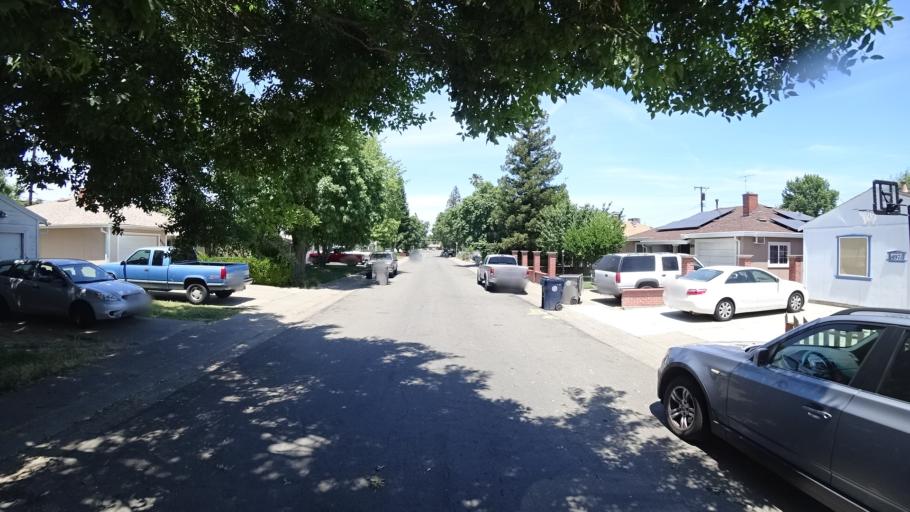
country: US
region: California
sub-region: Sacramento County
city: Florin
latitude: 38.5302
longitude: -121.4193
